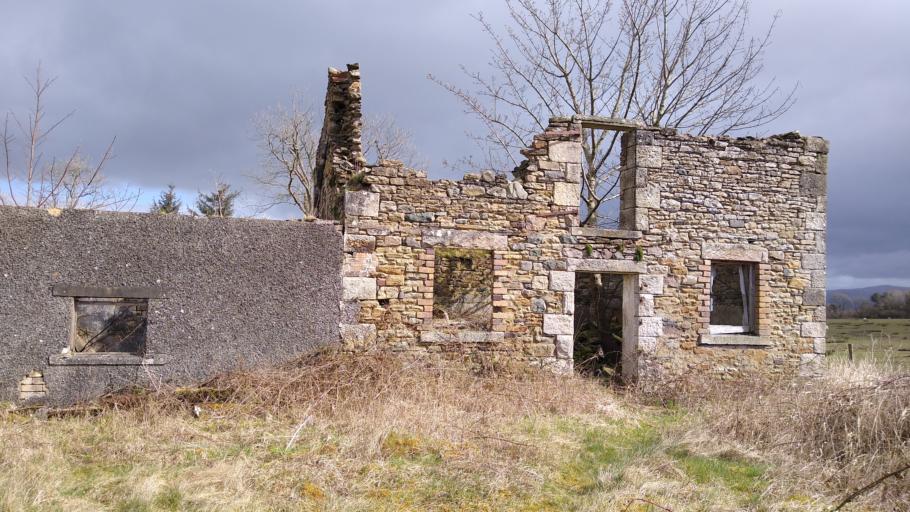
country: GB
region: England
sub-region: Cumbria
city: Dearham
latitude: 54.6909
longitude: -3.4399
